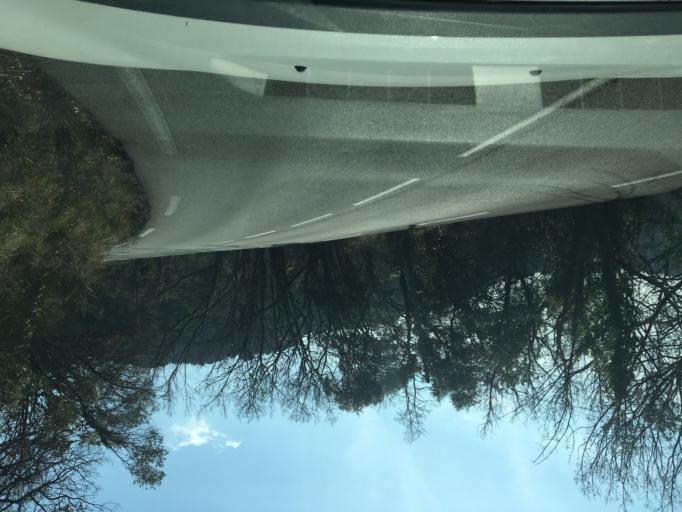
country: FR
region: Provence-Alpes-Cote d'Azur
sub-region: Departement du Var
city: Bargemon
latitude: 43.6061
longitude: 6.5518
